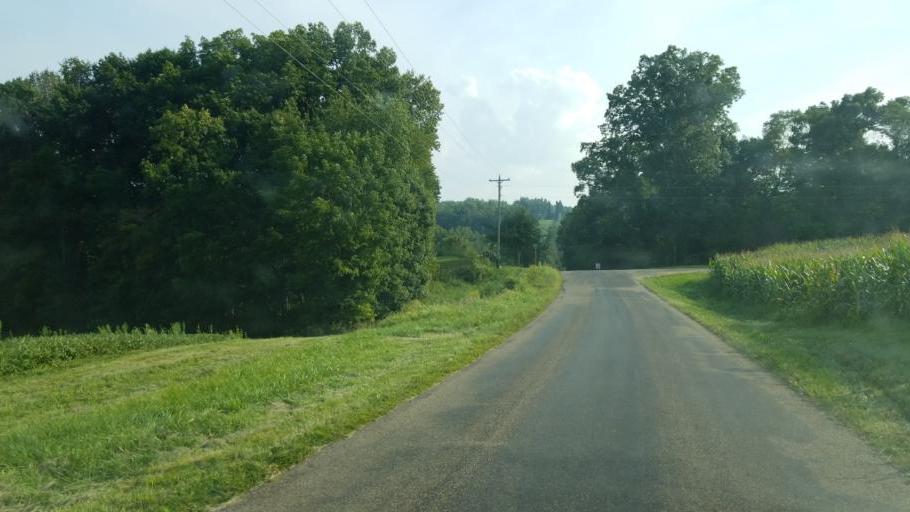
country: US
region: Ohio
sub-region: Knox County
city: Gambier
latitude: 40.3632
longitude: -82.4094
